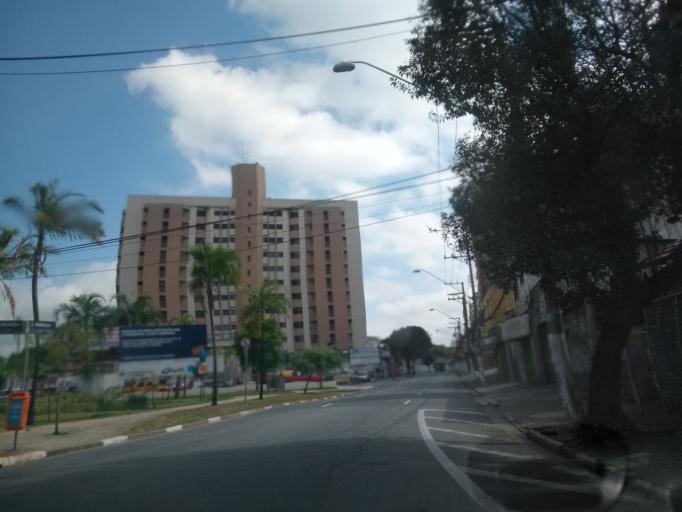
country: BR
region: Sao Paulo
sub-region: Sao Bernardo Do Campo
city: Sao Bernardo do Campo
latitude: -23.7130
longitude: -46.5530
